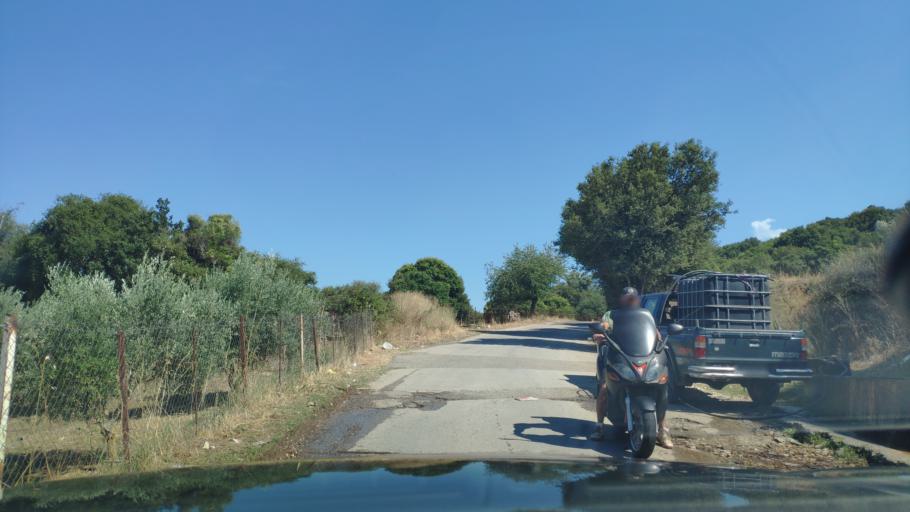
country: GR
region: West Greece
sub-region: Nomos Aitolias kai Akarnanias
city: Katouna
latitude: 38.8115
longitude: 21.1056
